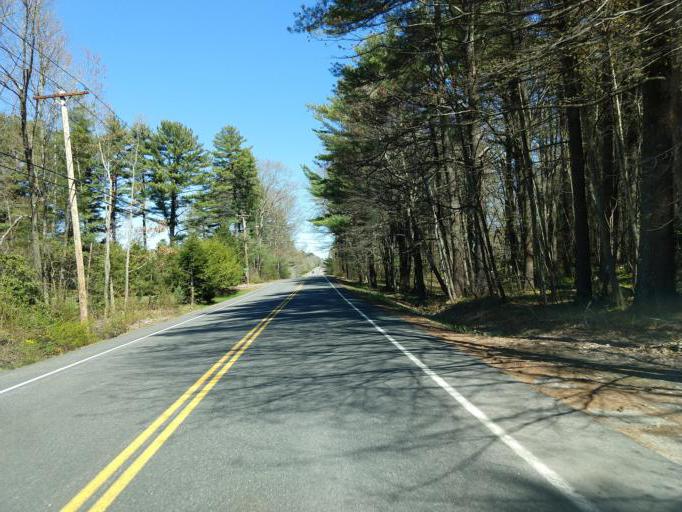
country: US
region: Maine
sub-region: York County
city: Kennebunk
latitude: 43.3479
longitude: -70.5492
